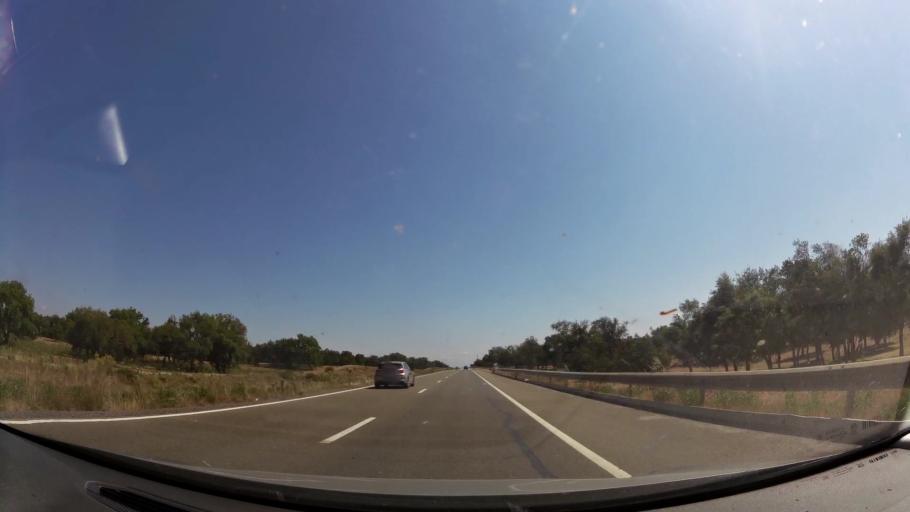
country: MA
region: Gharb-Chrarda-Beni Hssen
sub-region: Kenitra Province
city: Kenitra
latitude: 34.1507
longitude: -6.6790
